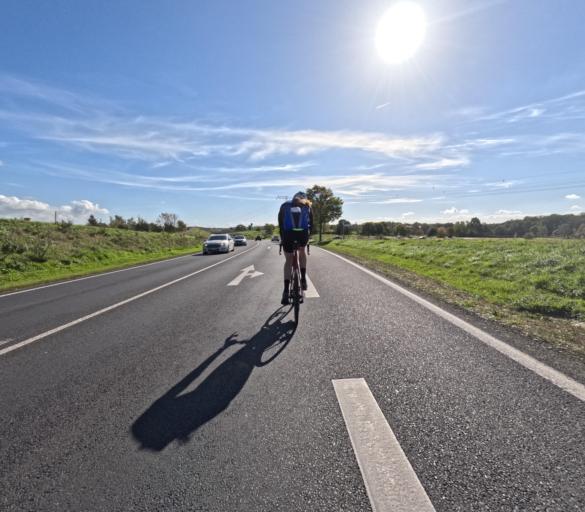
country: DE
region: Saxony
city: Moritzburg
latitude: 51.1400
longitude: 13.6530
